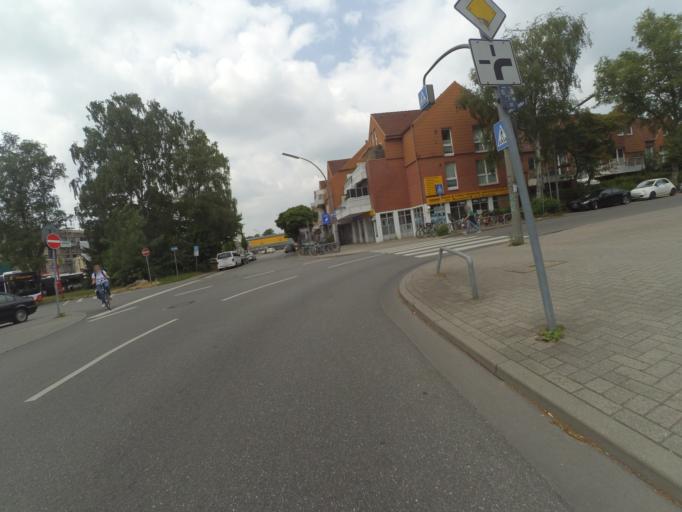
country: DE
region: Hamburg
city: Poppenbuettel
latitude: 53.6515
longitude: 10.0955
